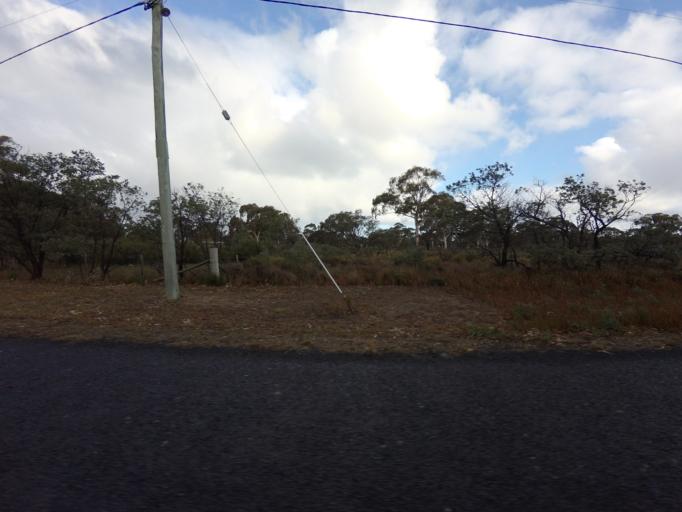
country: AU
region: Tasmania
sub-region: Break O'Day
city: St Helens
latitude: -42.1018
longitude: 148.0750
